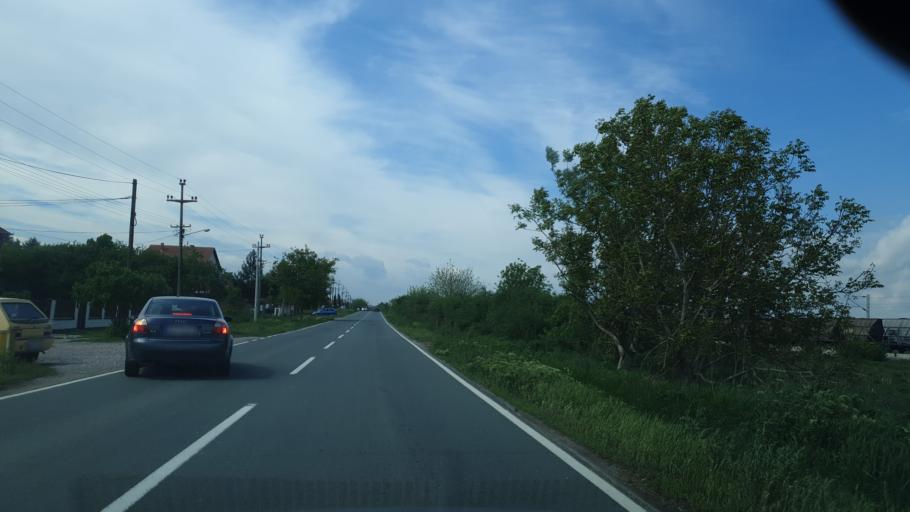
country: RS
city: Stubline
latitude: 44.5812
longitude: 20.1519
